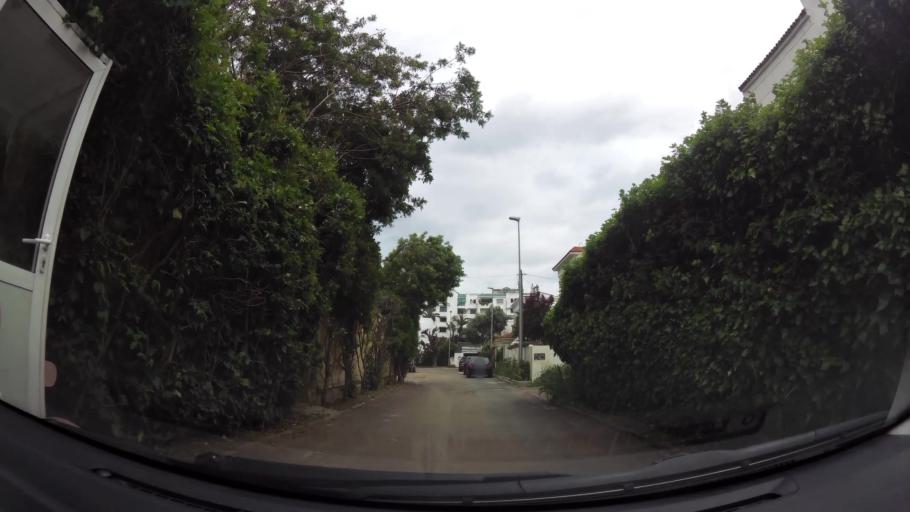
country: MA
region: Grand Casablanca
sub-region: Casablanca
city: Casablanca
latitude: 33.5753
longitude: -7.6533
